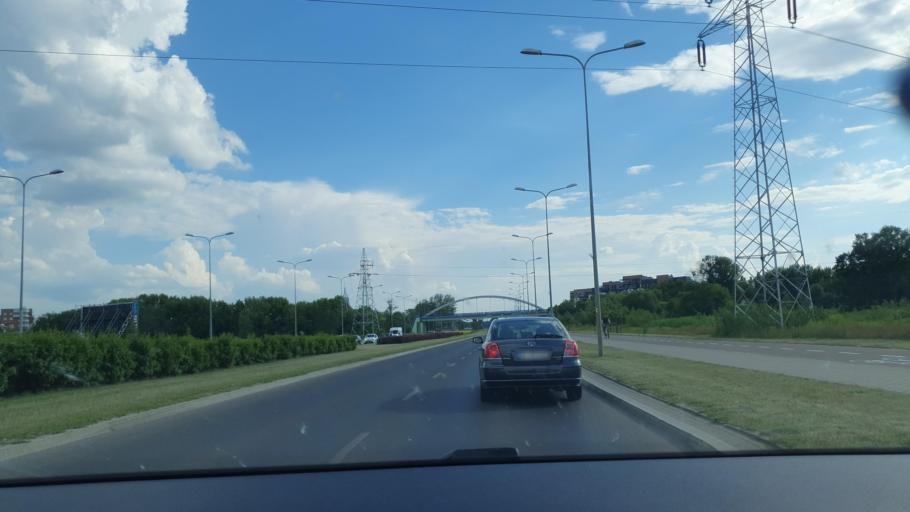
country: PL
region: Podlasie
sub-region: Bialystok
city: Bialystok
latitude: 53.1385
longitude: 23.1989
